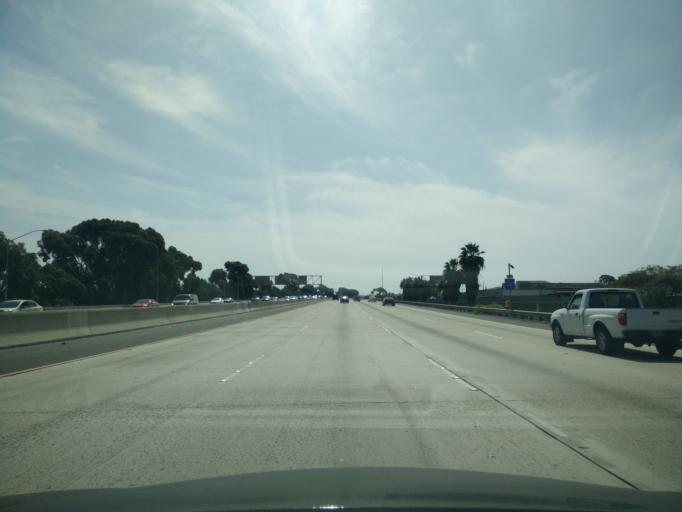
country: US
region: California
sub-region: San Diego County
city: National City
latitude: 32.6901
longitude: -117.1178
